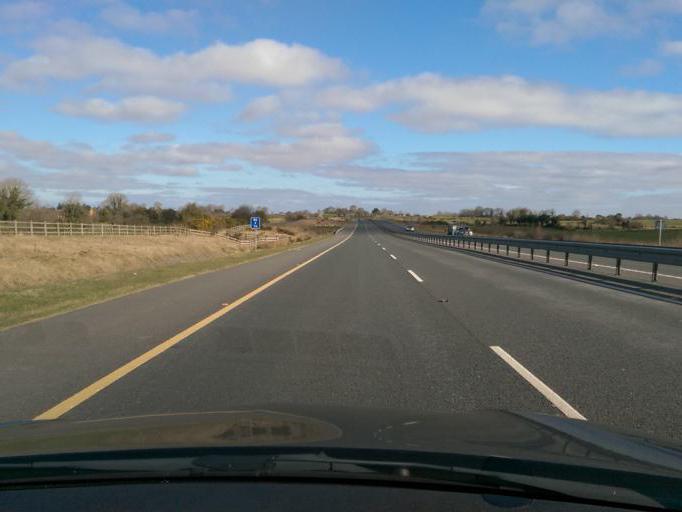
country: IE
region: Leinster
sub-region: An Iarmhi
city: Athlone
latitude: 53.3718
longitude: -8.0558
